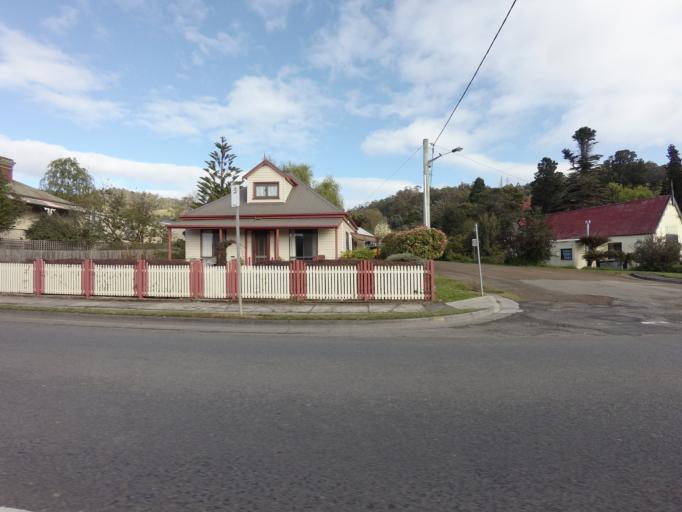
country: AU
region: Tasmania
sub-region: Huon Valley
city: Franklin
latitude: -43.0857
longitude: 147.0139
